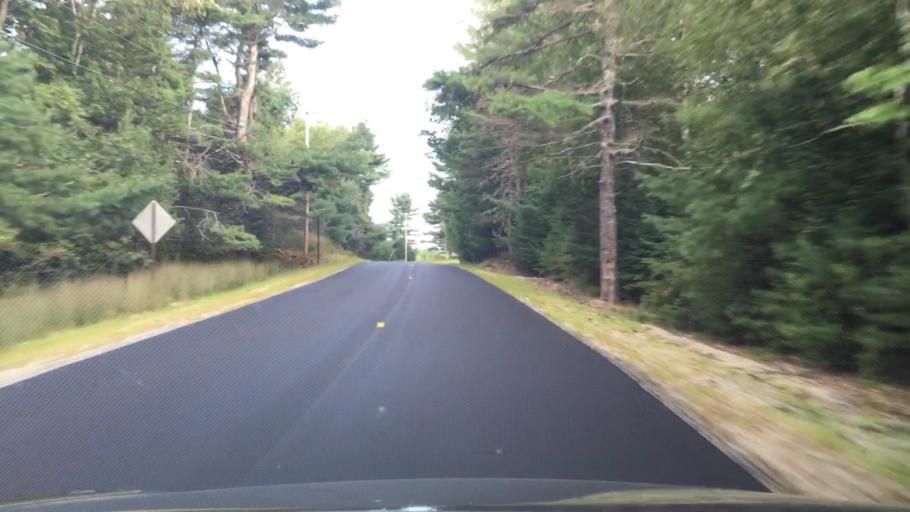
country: US
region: Maine
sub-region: Hancock County
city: Surry
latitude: 44.5170
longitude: -68.6060
